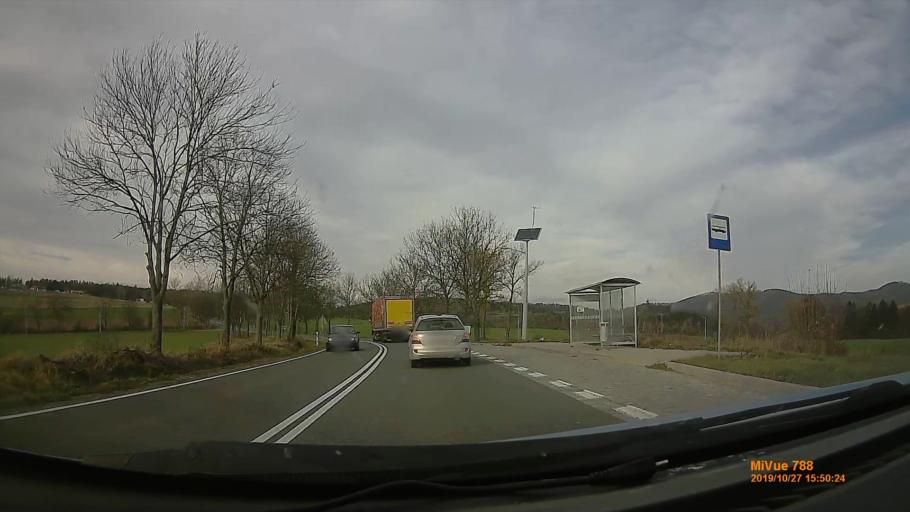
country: PL
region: Lower Silesian Voivodeship
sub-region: Powiat klodzki
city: Bozkow
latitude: 50.5170
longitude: 16.5853
